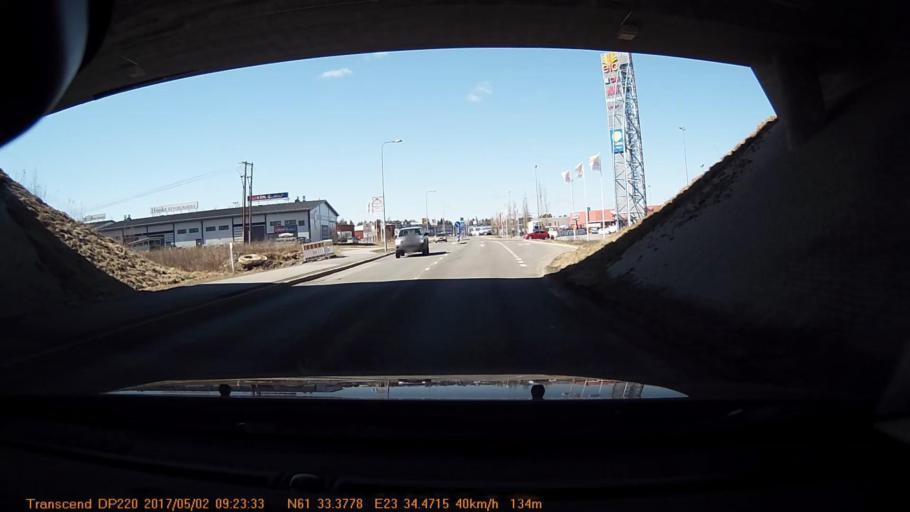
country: FI
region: Pirkanmaa
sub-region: Tampere
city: Yloejaervi
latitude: 61.5563
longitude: 23.5742
